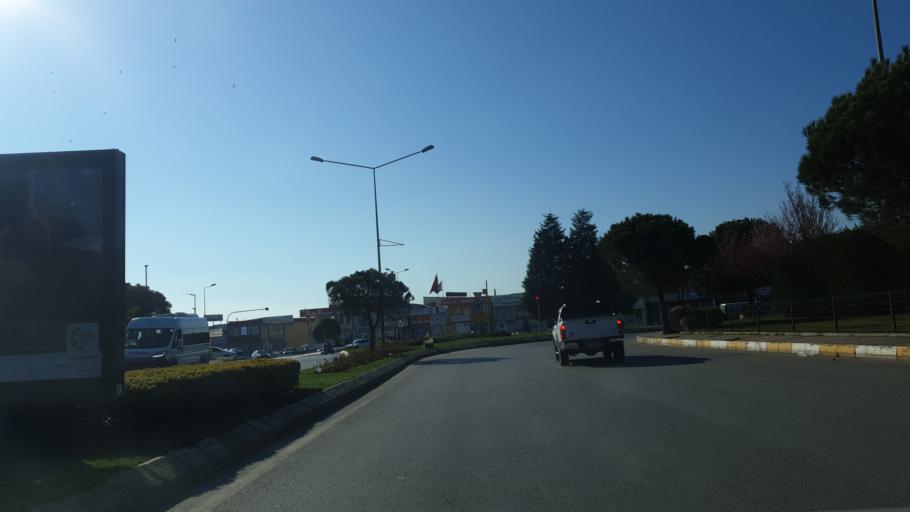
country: TR
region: Istanbul
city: Icmeler
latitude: 40.8815
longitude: 29.3479
